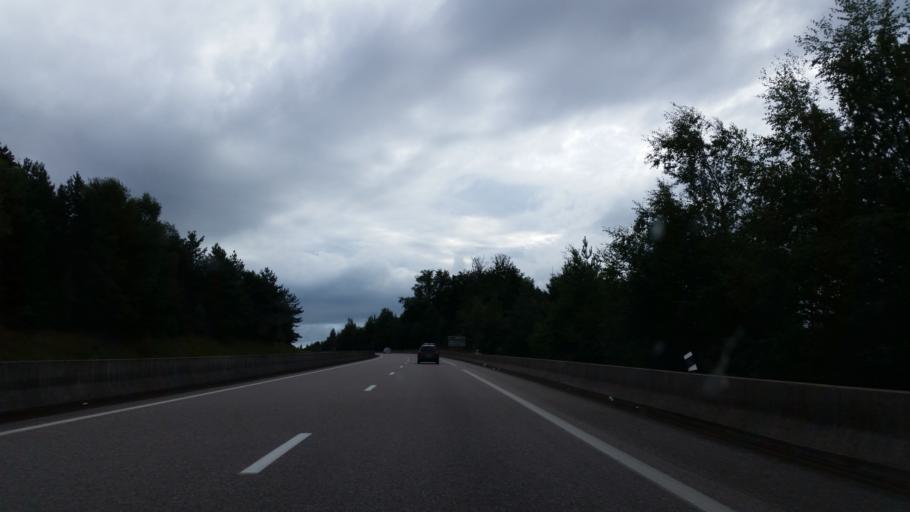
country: FR
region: Lorraine
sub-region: Departement des Vosges
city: Remiremont
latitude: 48.0091
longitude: 6.5596
